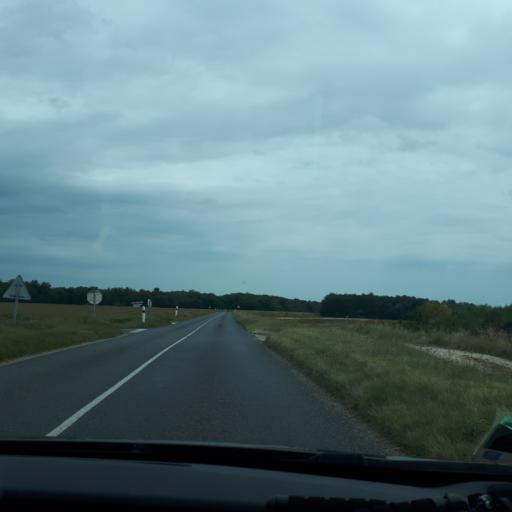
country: FR
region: Centre
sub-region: Departement du Loiret
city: Sully-sur-Loire
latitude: 47.7758
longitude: 2.3873
